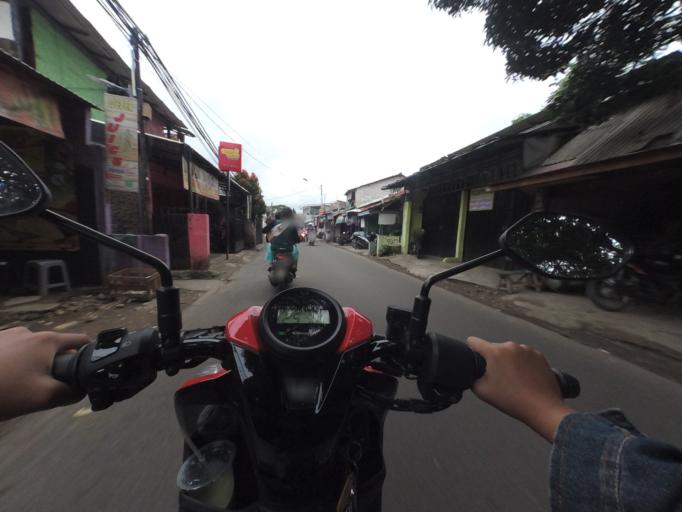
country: ID
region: West Java
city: Bogor
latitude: -6.5639
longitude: 106.8021
